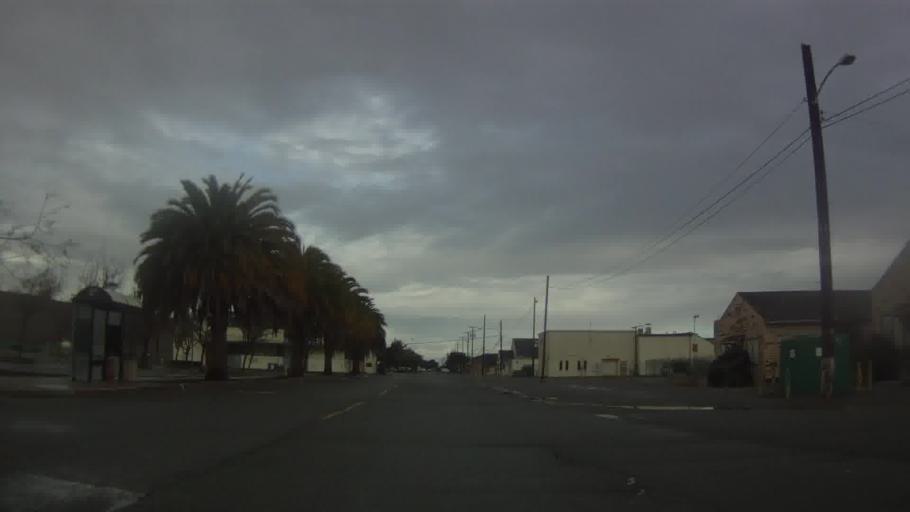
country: US
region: California
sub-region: San Francisco County
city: San Francisco
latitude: 37.8219
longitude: -122.3677
